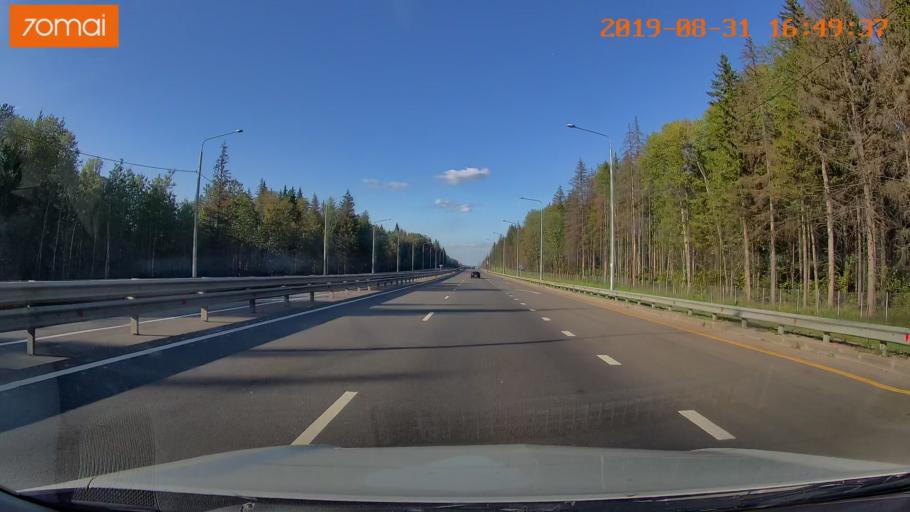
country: RU
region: Kaluga
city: Pyatovskiy
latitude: 54.6938
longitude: 36.1562
